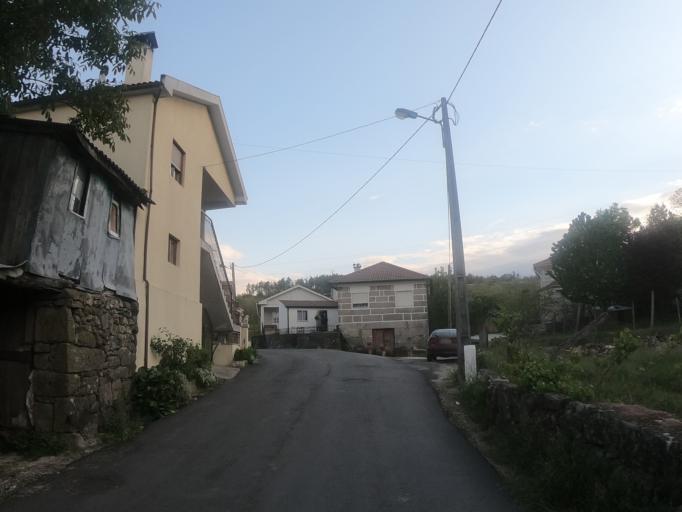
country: PT
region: Vila Real
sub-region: Santa Marta de Penaguiao
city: Santa Marta de Penaguiao
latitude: 41.2793
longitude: -7.8156
